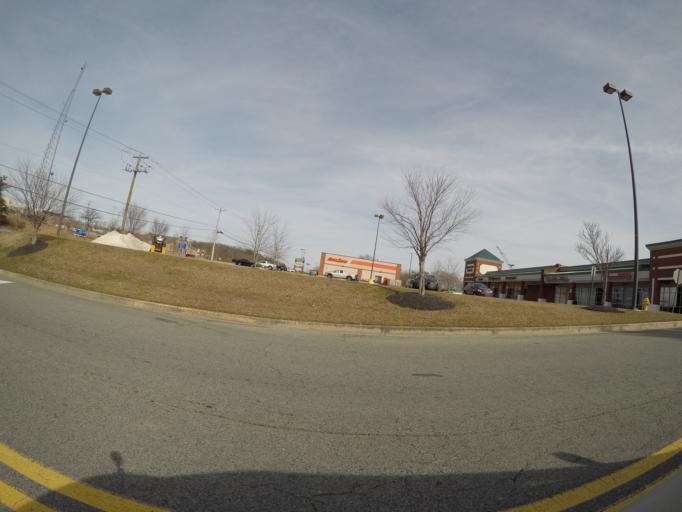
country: US
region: Maryland
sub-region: Cecil County
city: North East
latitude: 39.6067
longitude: -75.9513
